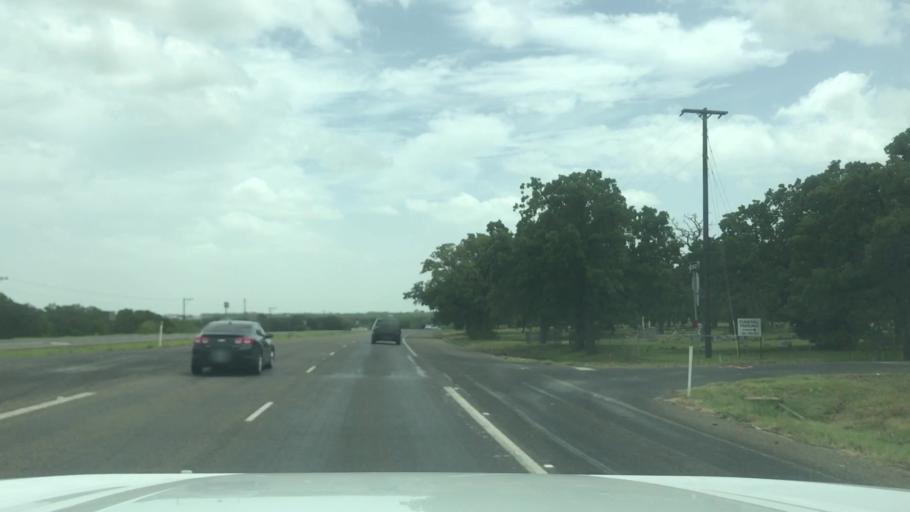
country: US
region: Texas
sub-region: McLennan County
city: Riesel
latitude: 31.4923
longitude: -96.9302
